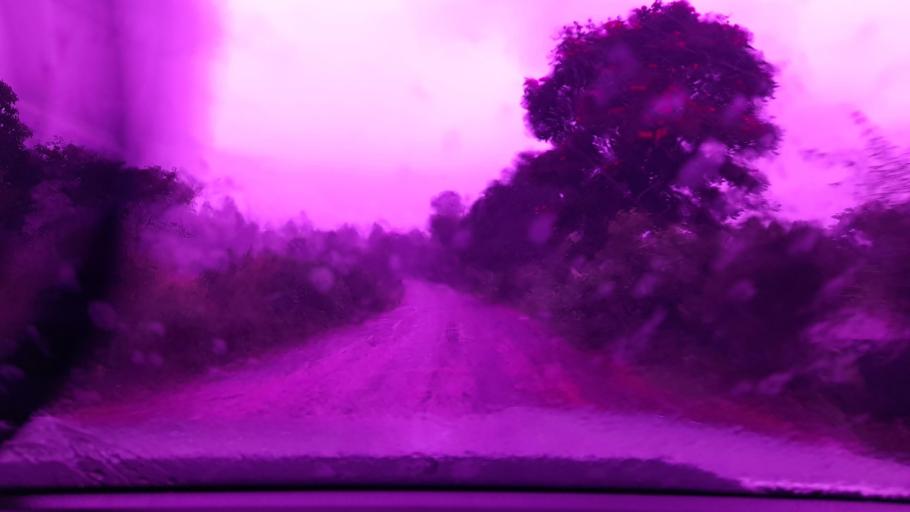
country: ET
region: Oromiya
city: Metu
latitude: 8.3696
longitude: 35.5966
